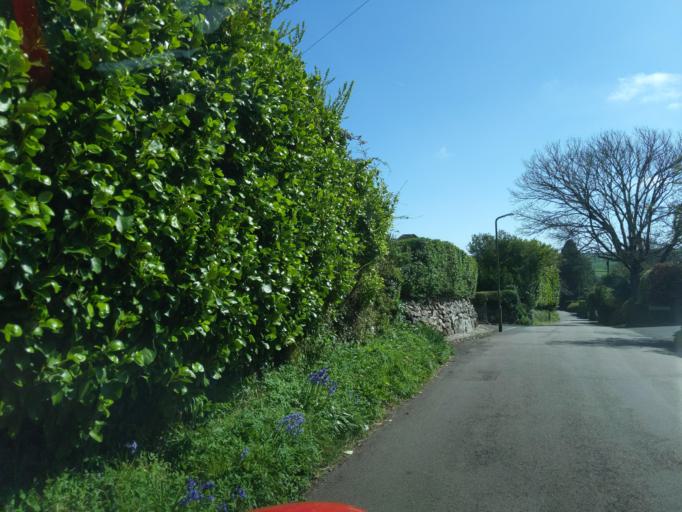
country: GB
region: England
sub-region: Borough of Torbay
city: Paignton
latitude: 50.3996
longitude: -3.5668
